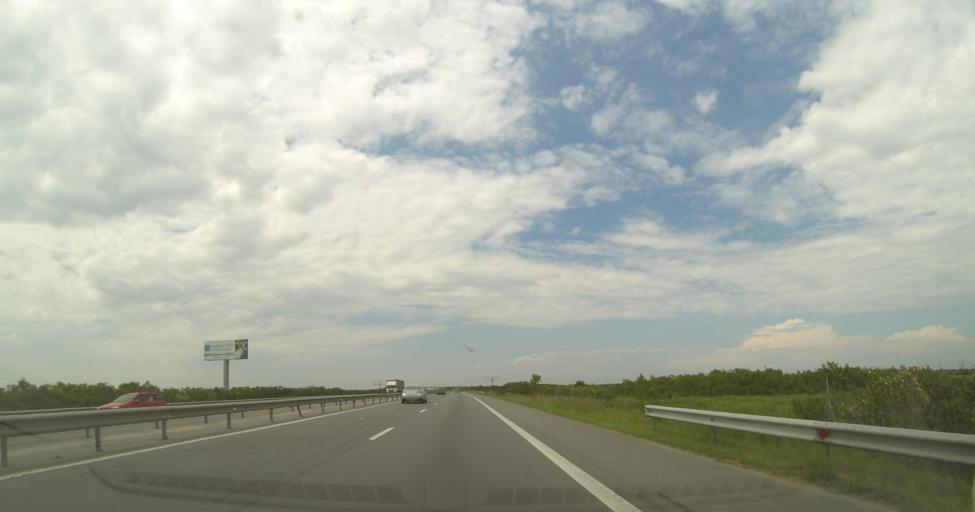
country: RO
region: Dambovita
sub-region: Comuna Uliesti
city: Uliesti
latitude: 44.6175
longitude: 25.4422
